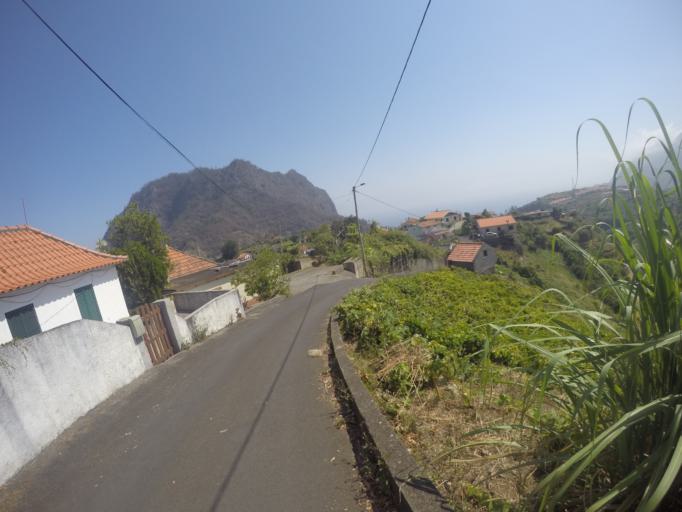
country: PT
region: Madeira
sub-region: Santana
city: Santana
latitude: 32.7580
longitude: -16.8439
